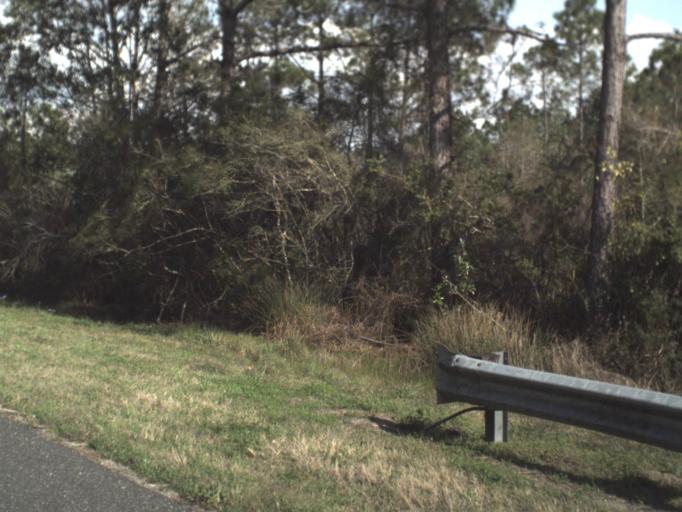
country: US
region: Florida
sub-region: Bay County
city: Youngstown
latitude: 30.2783
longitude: -85.5153
